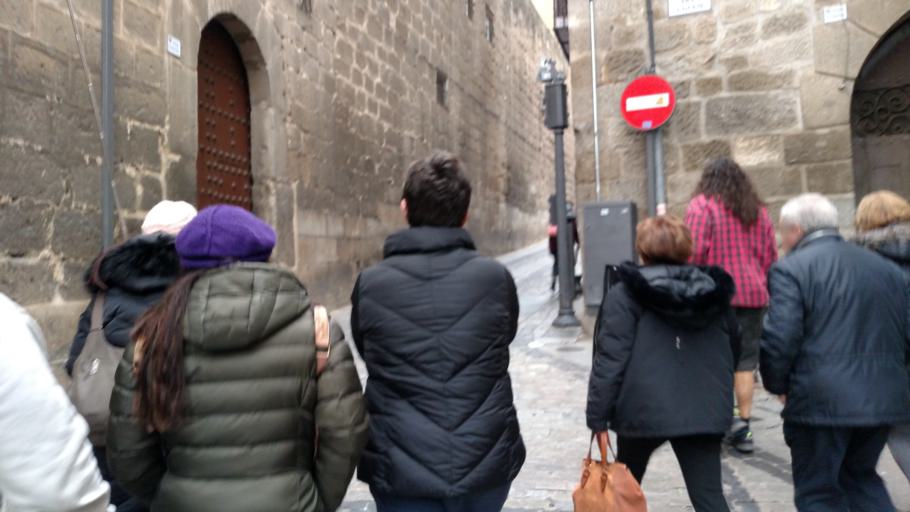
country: ES
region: Castille-La Mancha
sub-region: Province of Toledo
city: Toledo
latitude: 39.8570
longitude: -4.0227
